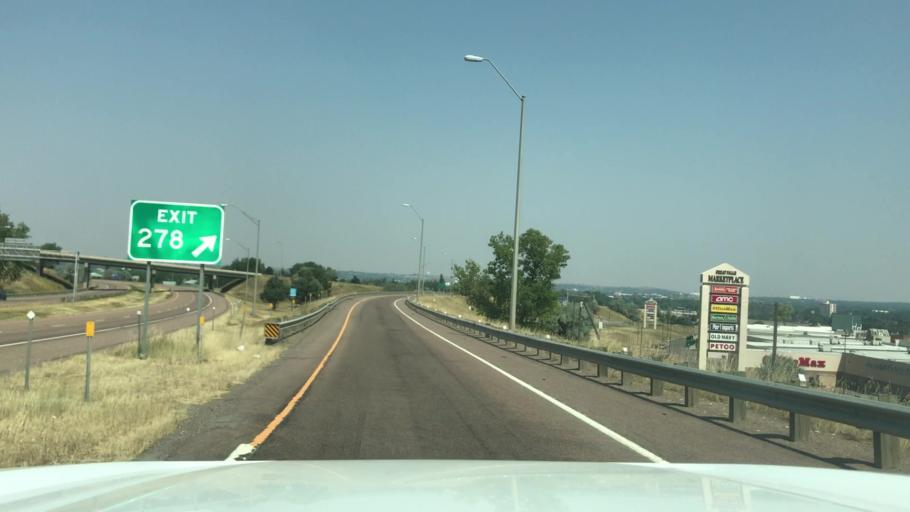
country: US
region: Montana
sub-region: Cascade County
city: Great Falls
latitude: 47.4827
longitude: -111.3462
